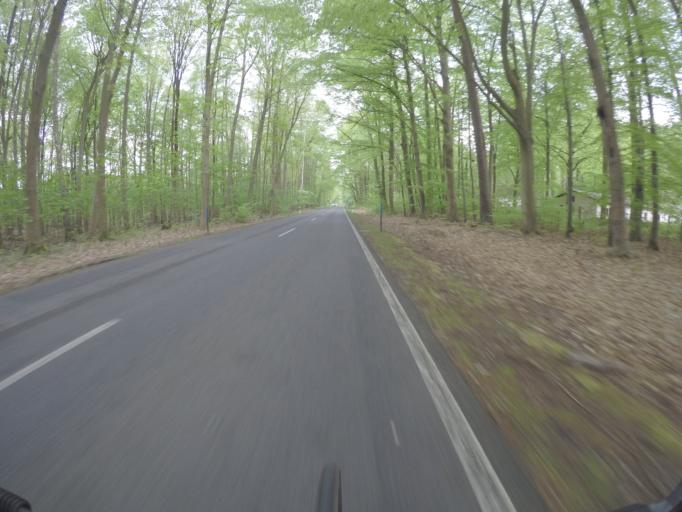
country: DE
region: Brandenburg
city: Joachimsthal
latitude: 52.9255
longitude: 13.7325
